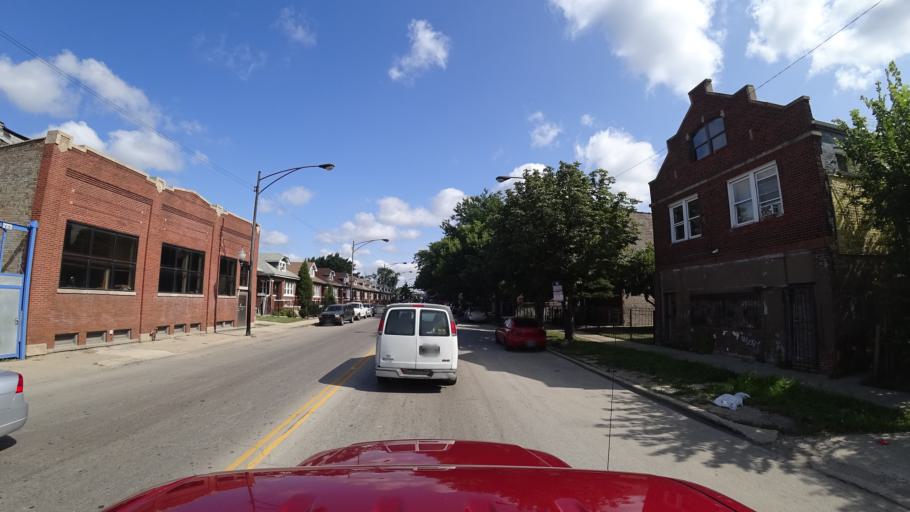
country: US
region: Illinois
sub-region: Cook County
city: Cicero
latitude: 41.8336
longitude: -87.7243
